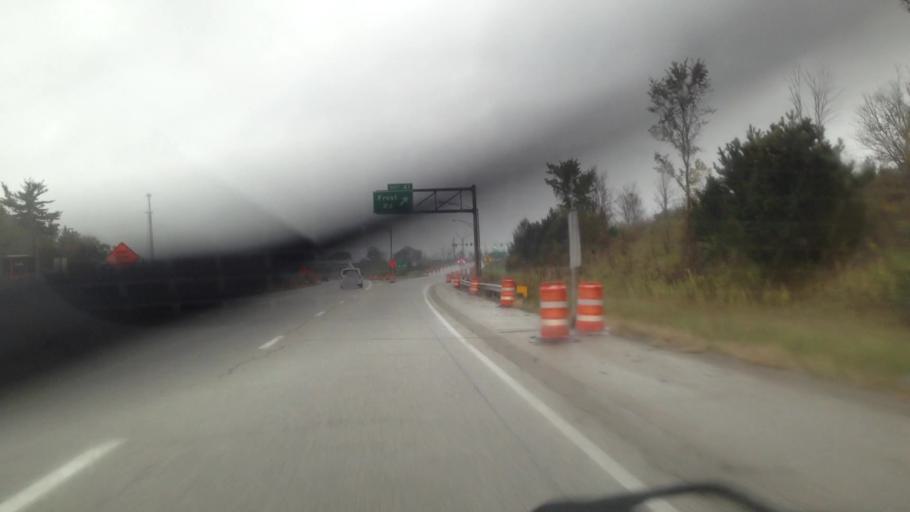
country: US
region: Ohio
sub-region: Portage County
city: Streetsboro
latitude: 41.2586
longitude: -81.3742
